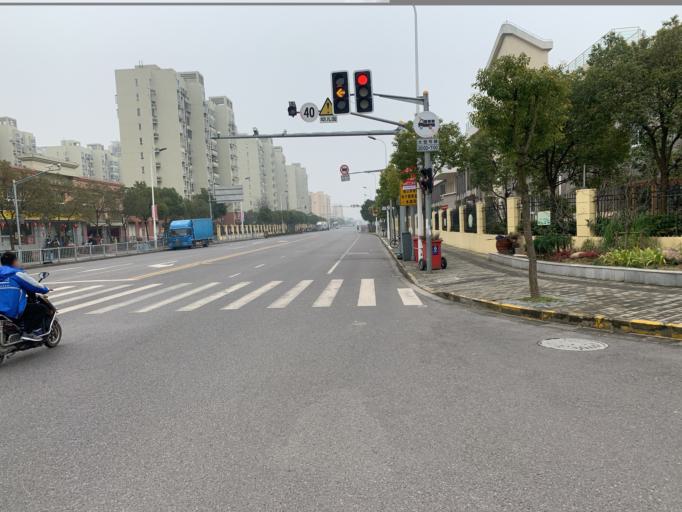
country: CN
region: Shanghai Shi
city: Huamu
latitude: 31.2412
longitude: 121.6249
